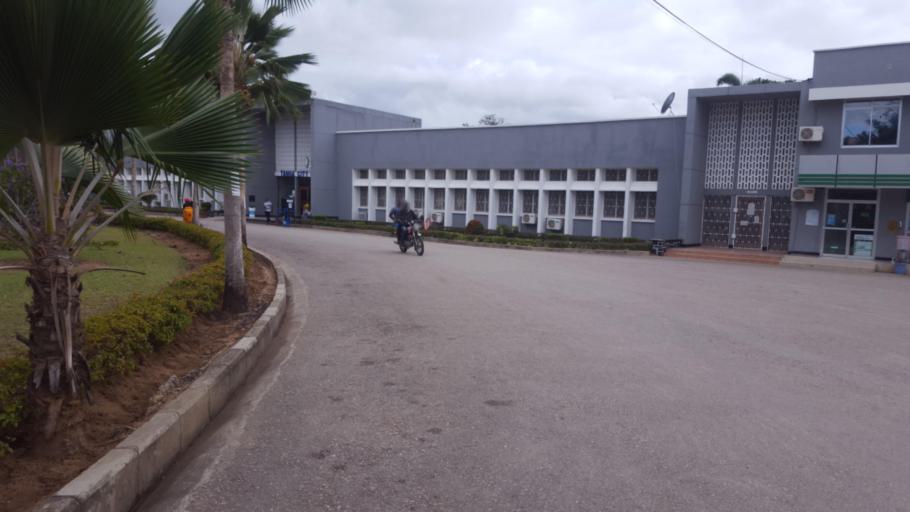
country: TZ
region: Tanga
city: Tanga
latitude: -5.0696
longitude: 39.0979
